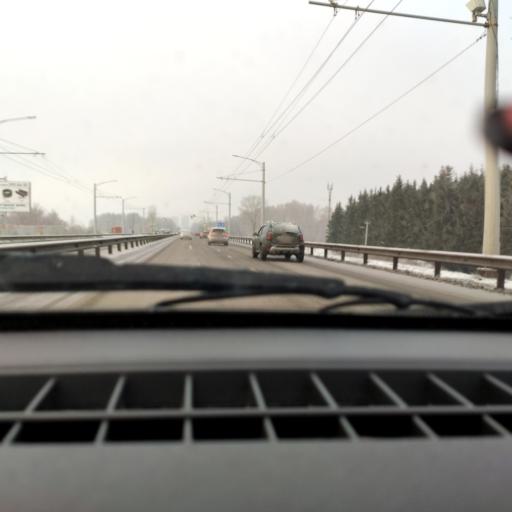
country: RU
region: Bashkortostan
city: Ufa
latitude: 54.7668
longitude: 55.9410
